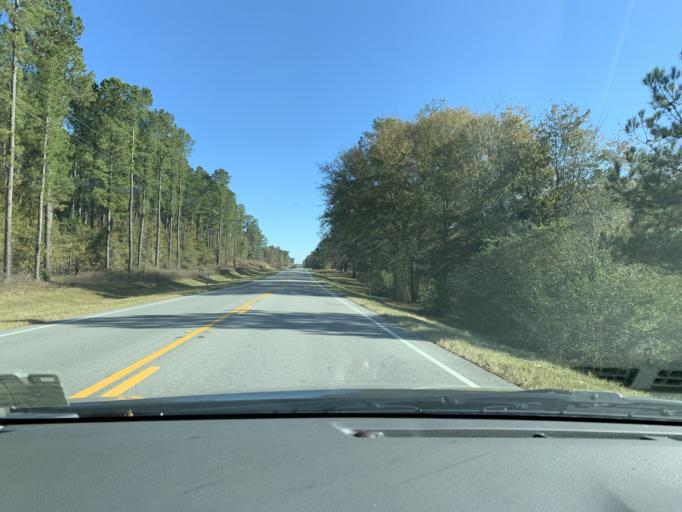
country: US
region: Georgia
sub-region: Ben Hill County
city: Fitzgerald
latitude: 31.7367
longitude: -83.1624
